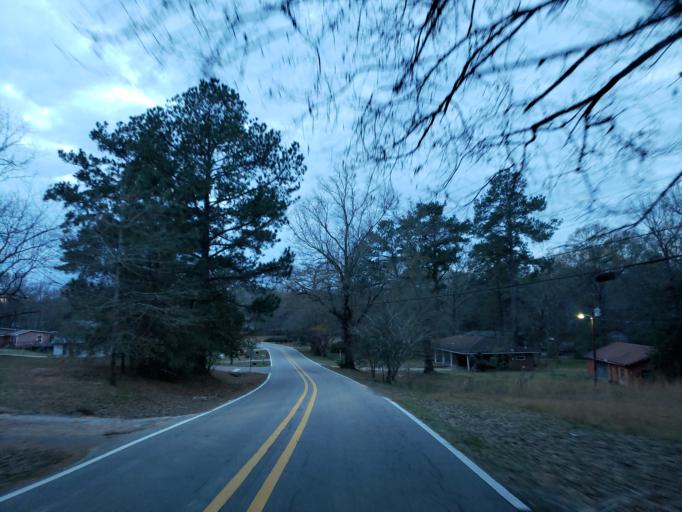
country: US
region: Mississippi
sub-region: Forrest County
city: Petal
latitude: 31.3393
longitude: -89.2544
